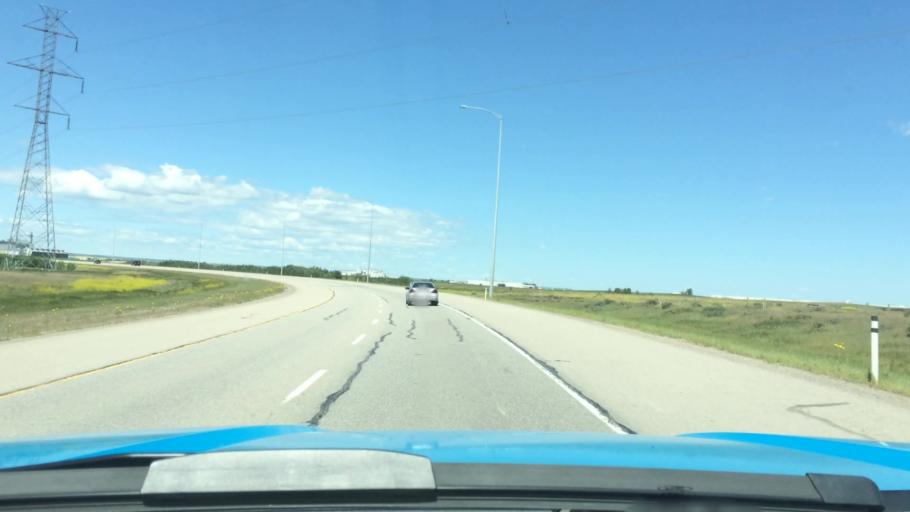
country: CA
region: Alberta
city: Airdrie
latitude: 51.1763
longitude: -113.9157
